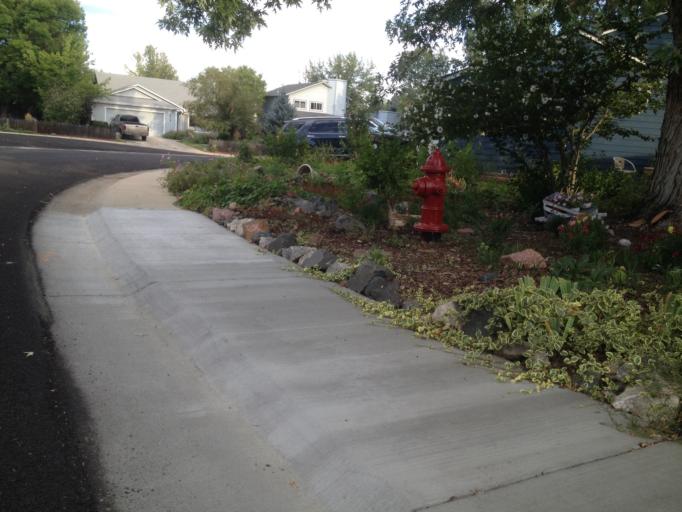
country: US
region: Colorado
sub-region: Boulder County
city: Louisville
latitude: 39.9720
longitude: -105.1370
